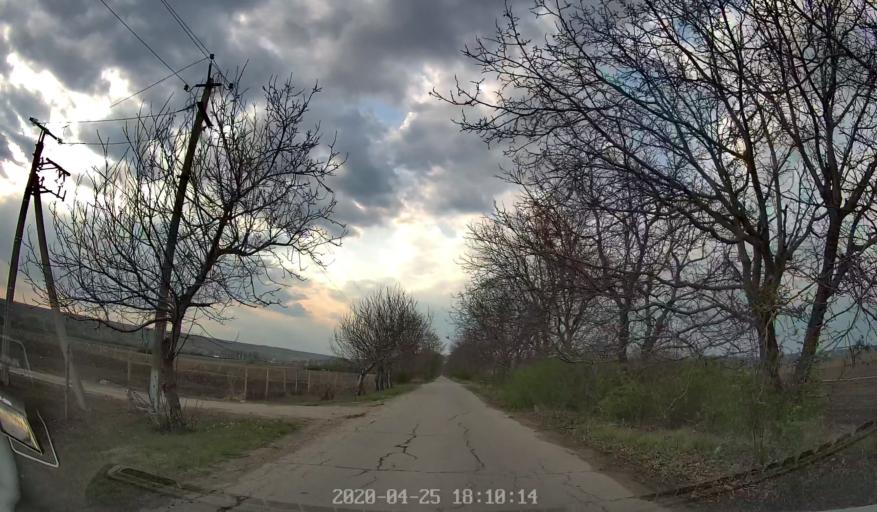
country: MD
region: Chisinau
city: Vadul lui Voda
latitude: 47.1328
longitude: 29.0778
